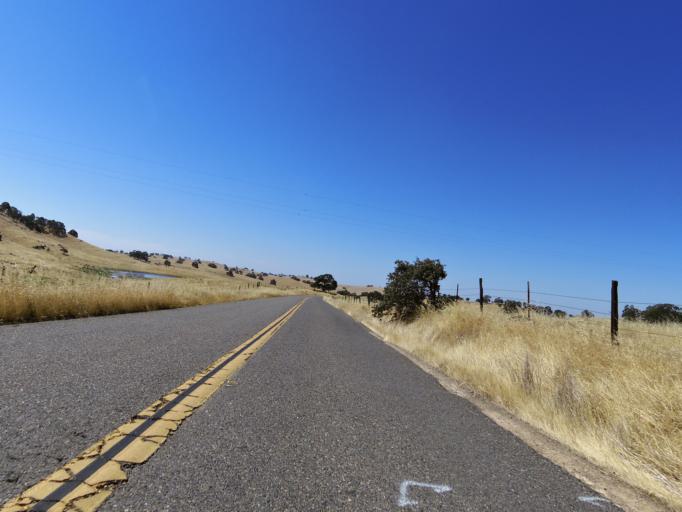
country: US
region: California
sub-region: Merced County
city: Planada
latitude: 37.5772
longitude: -120.3075
